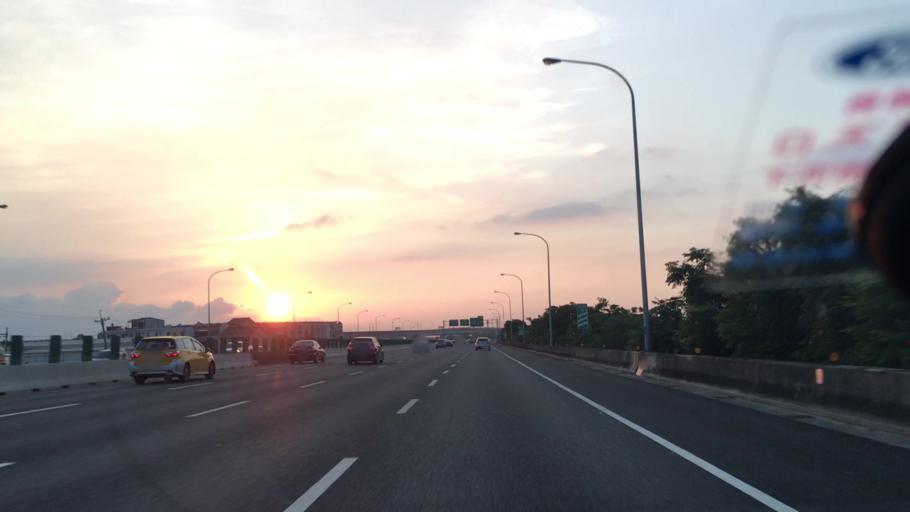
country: TW
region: Taiwan
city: Taoyuan City
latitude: 25.0308
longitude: 121.2468
